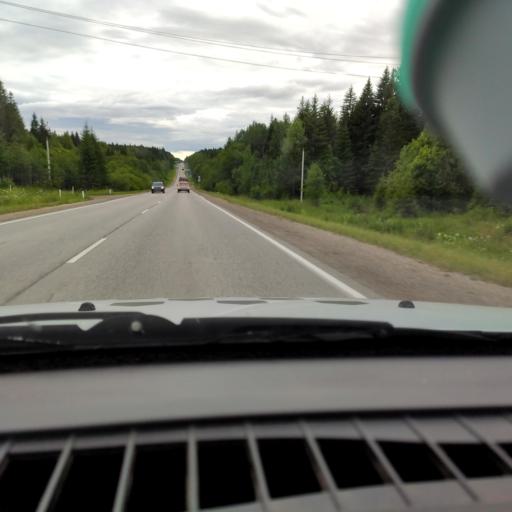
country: RU
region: Perm
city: Lys'va
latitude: 58.1181
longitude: 57.7097
